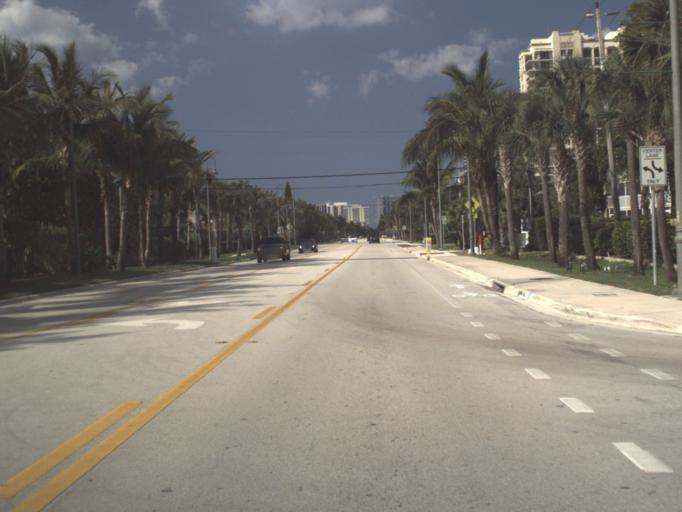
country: US
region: Florida
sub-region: Palm Beach County
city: Palm Beach Shores
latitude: 26.7894
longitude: -80.0347
